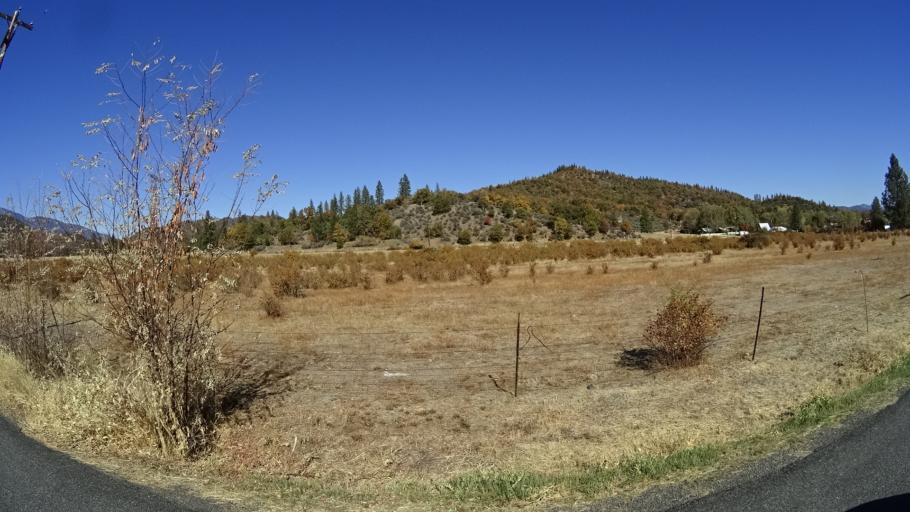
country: US
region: California
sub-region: Siskiyou County
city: Yreka
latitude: 41.5484
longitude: -122.9121
